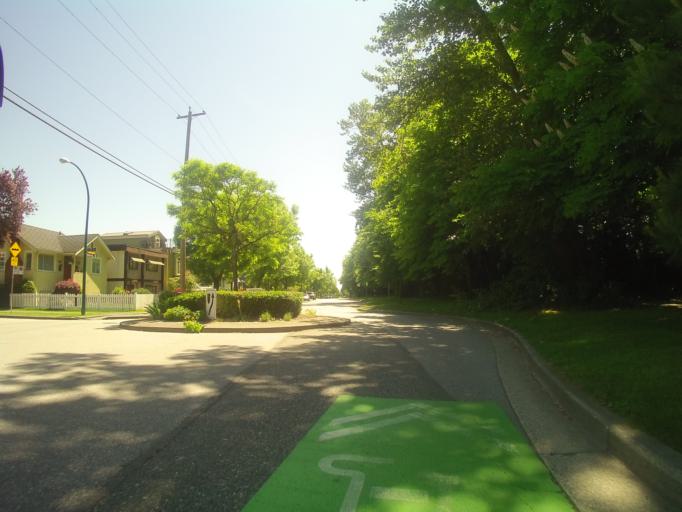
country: CA
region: British Columbia
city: Vancouver
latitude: 49.2231
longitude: -123.1061
